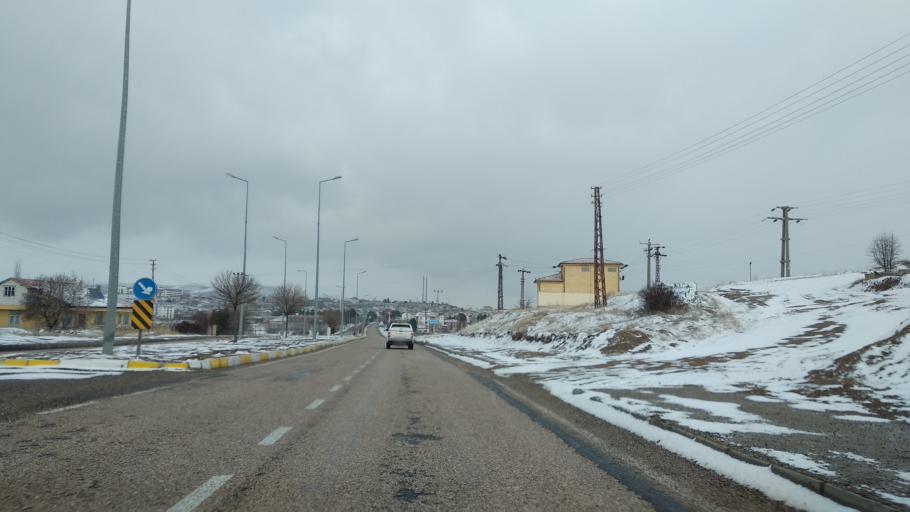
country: TR
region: Kayseri
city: Pinarbasi
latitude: 38.7138
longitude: 36.3804
